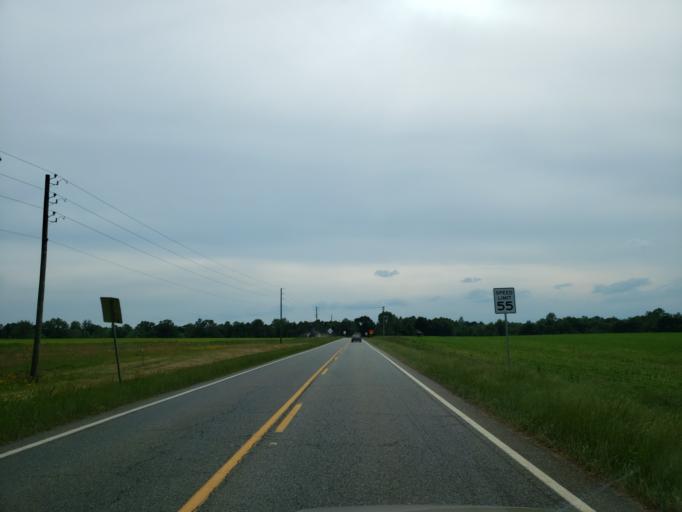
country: US
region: Georgia
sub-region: Macon County
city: Marshallville
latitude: 32.3677
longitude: -83.9010
